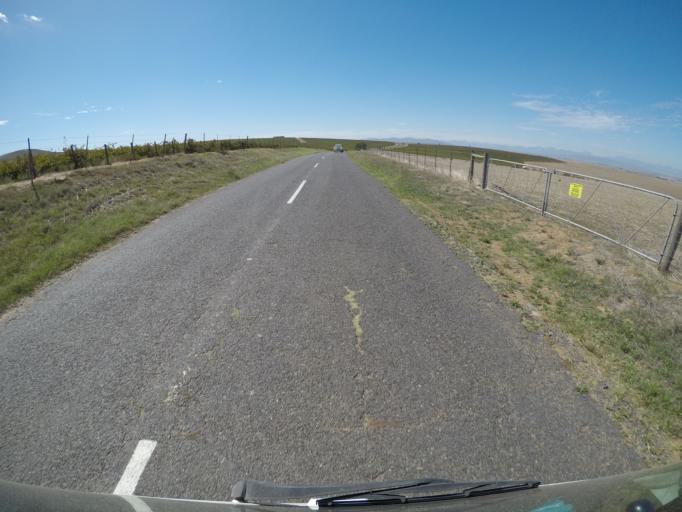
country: ZA
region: Western Cape
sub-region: City of Cape Town
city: Sunset Beach
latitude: -33.7216
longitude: 18.5736
